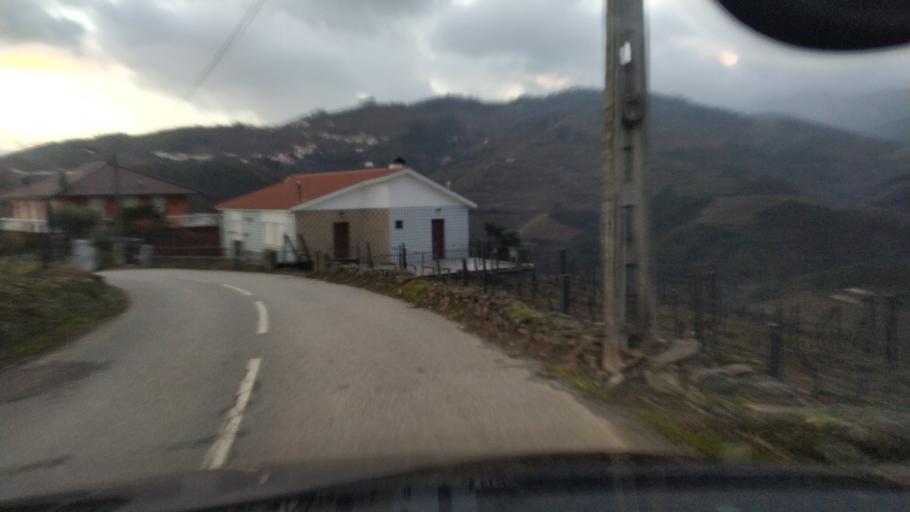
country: PT
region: Vila Real
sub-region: Santa Marta de Penaguiao
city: Santa Marta de Penaguiao
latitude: 41.2387
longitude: -7.7728
